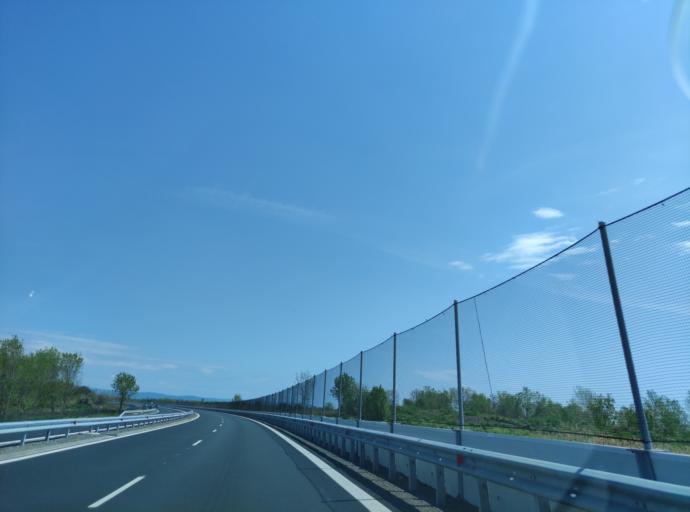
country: BG
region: Burgas
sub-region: Obshtina Pomorie
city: Pomorie
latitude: 42.5920
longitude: 27.6112
